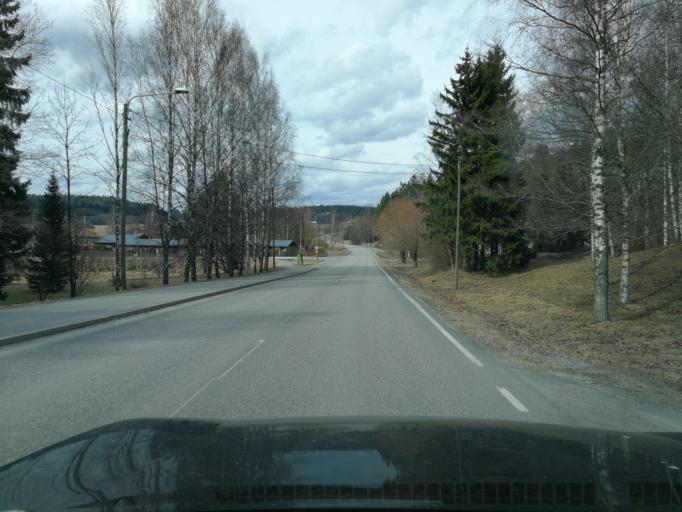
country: FI
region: Uusimaa
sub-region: Helsinki
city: Siuntio
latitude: 60.1771
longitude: 24.2029
